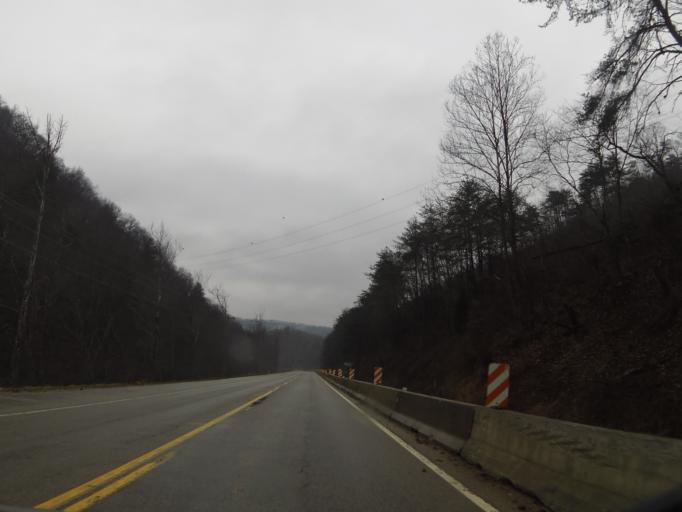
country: US
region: Tennessee
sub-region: Morgan County
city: Coalfield
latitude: 35.9833
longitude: -84.4817
